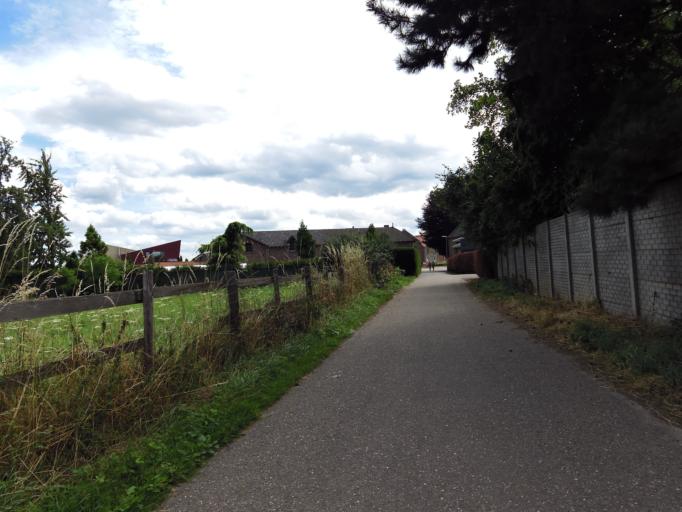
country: NL
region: Limburg
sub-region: Gemeente Schinnen
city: Doenrade
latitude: 50.9735
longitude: 5.8880
